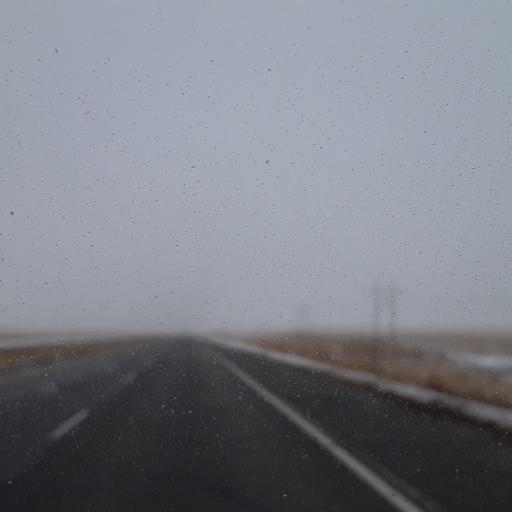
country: US
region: Nebraska
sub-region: Cheyenne County
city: Sidney
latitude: 40.7934
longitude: -102.8842
